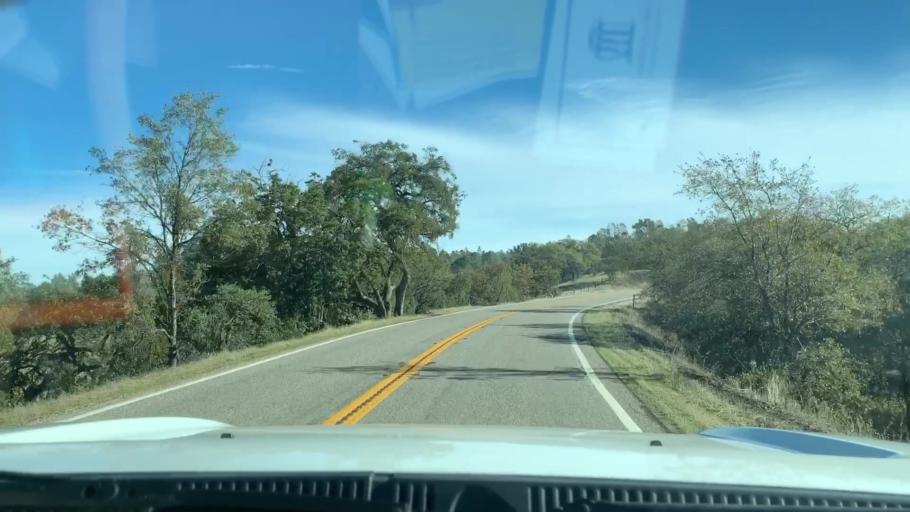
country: US
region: California
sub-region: Monterey County
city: King City
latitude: 36.1938
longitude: -120.7690
